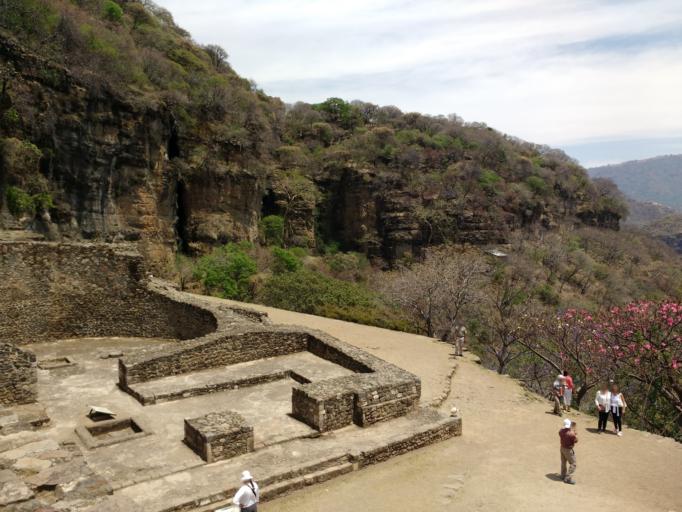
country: MX
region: Mexico
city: Malinalco
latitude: 18.9532
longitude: -99.5030
